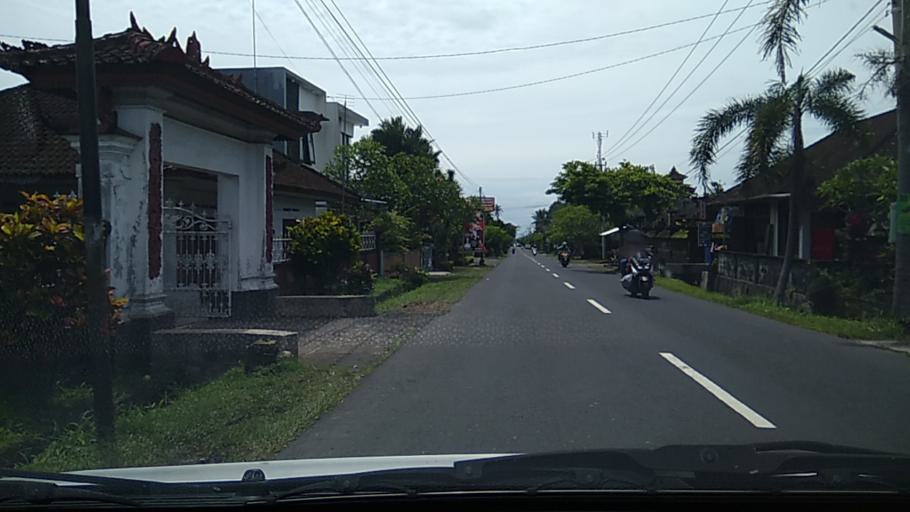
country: ID
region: Bali
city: Wanasari Baleran
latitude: -8.4767
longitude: 115.1363
